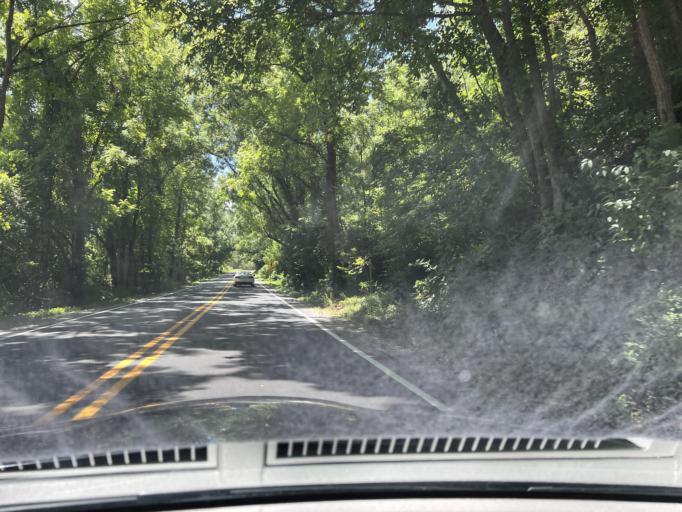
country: US
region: North Carolina
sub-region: Buncombe County
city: Fairview
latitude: 35.4893
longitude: -82.4326
